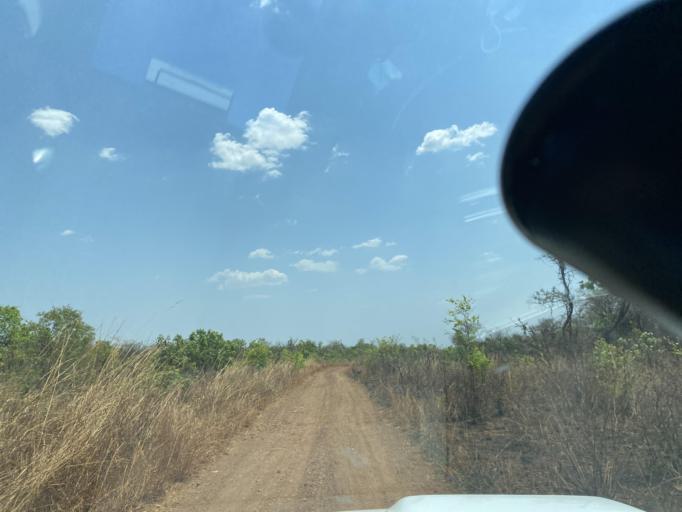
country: ZM
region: Lusaka
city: Lusaka
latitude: -15.5080
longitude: 27.9850
